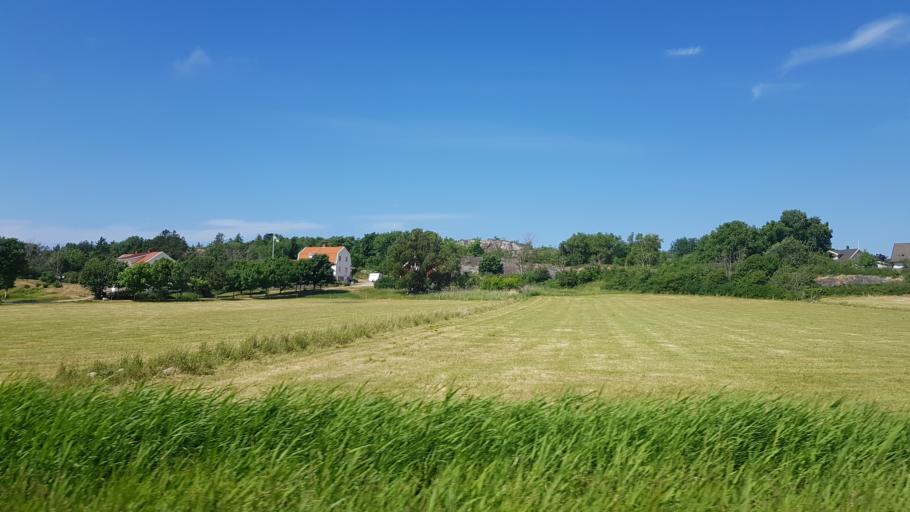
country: SE
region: Vaestra Goetaland
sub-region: Tjorns Kommun
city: Skaerhamn
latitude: 57.9817
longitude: 11.5665
